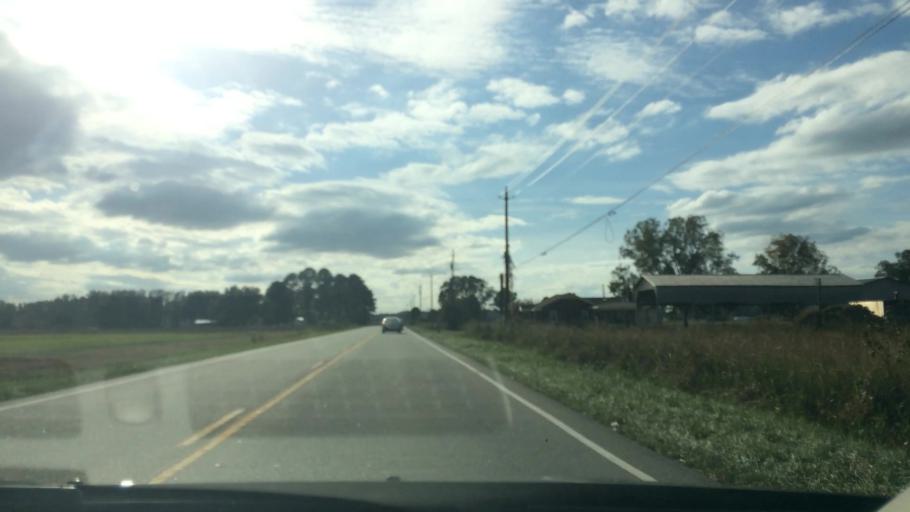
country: US
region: North Carolina
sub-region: Wayne County
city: Elroy
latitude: 35.4309
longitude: -77.8759
